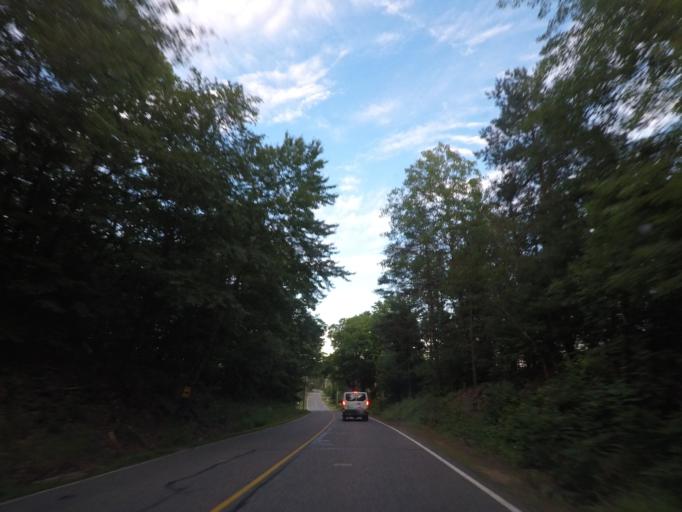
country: US
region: Massachusetts
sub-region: Worcester County
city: Warren
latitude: 42.1762
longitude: -72.1591
